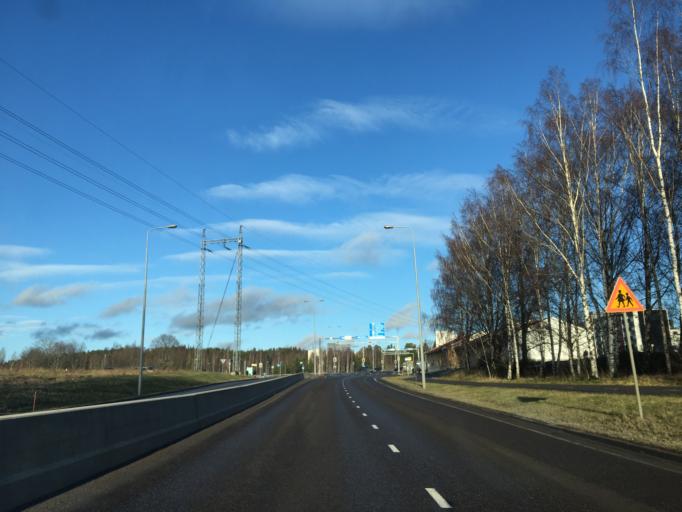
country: FI
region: Varsinais-Suomi
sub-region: Turku
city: Raisio
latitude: 60.4585
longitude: 22.1953
